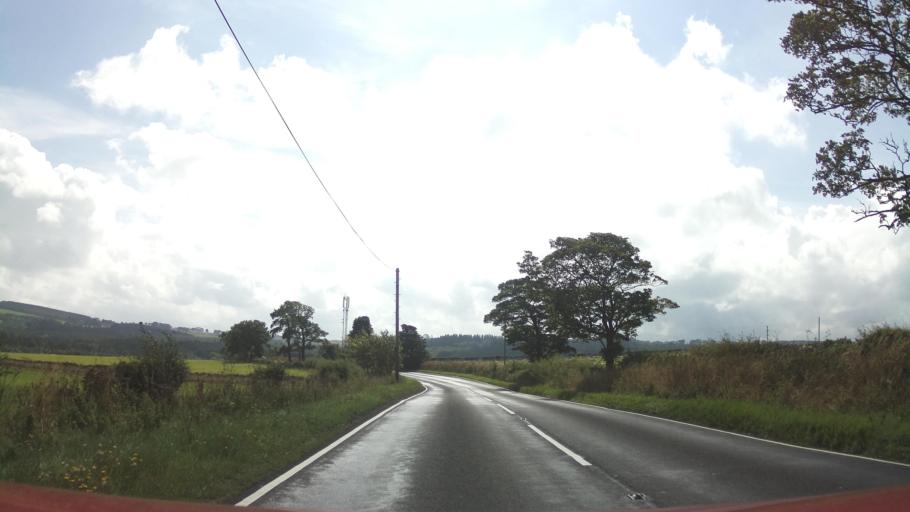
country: GB
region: England
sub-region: Northumberland
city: Healey
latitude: 54.9135
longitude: -1.9546
